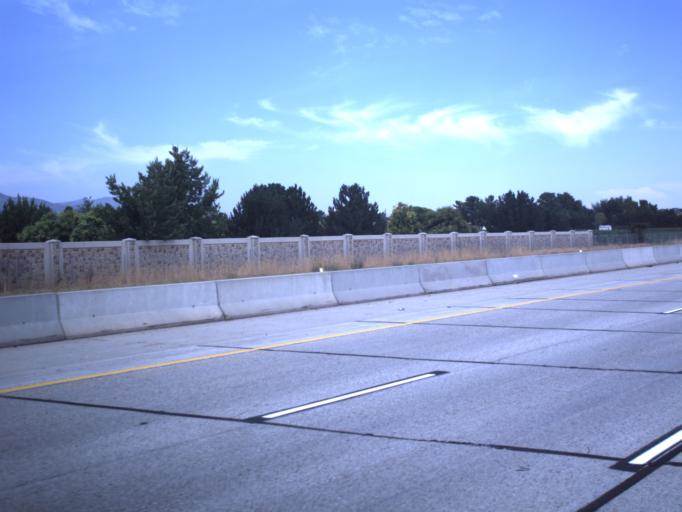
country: US
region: Utah
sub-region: Salt Lake County
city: Riverton
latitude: 40.5296
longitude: -111.9840
